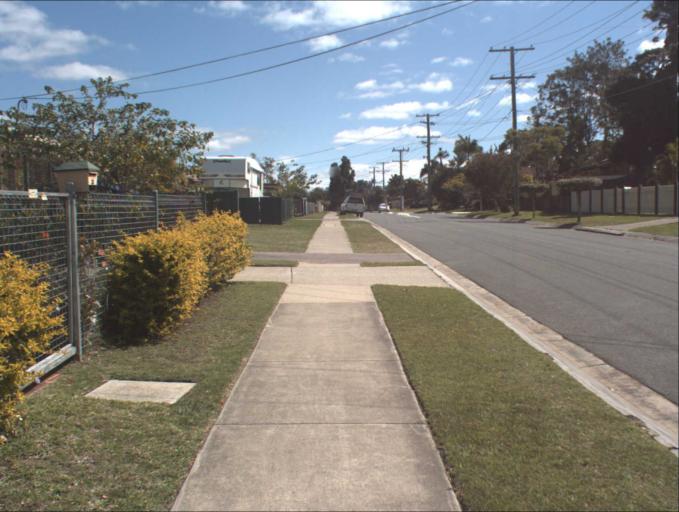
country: AU
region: Queensland
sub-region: Logan
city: Logan Reserve
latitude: -27.6891
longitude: 153.0868
